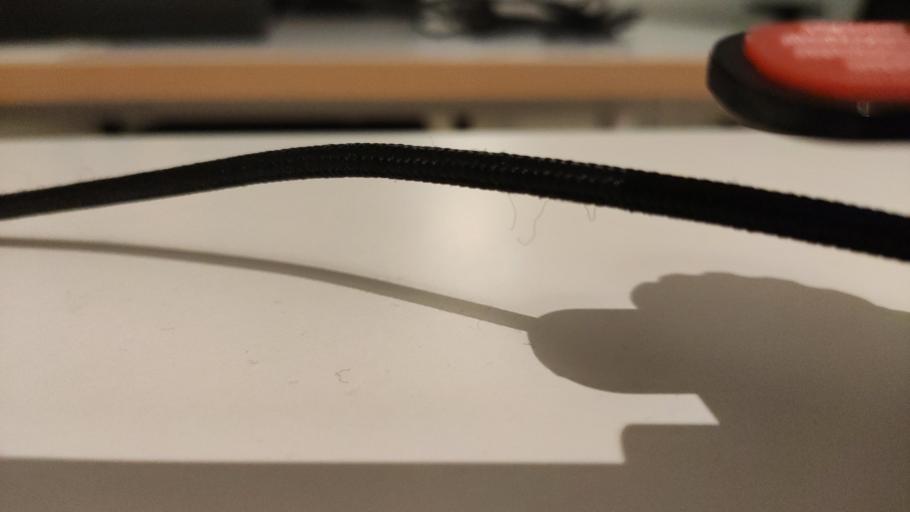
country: RU
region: Moskovskaya
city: Ol'yavidovo
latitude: 56.4210
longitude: 37.7349
